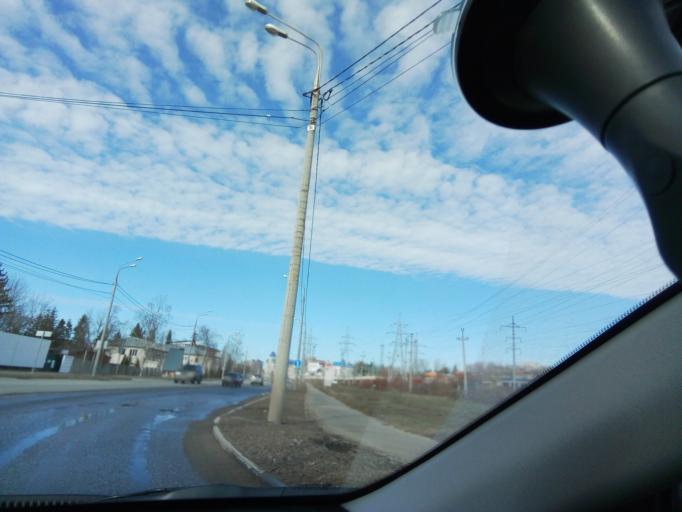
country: RU
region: Chuvashia
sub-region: Cheboksarskiy Rayon
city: Cheboksary
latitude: 56.1075
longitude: 47.2450
